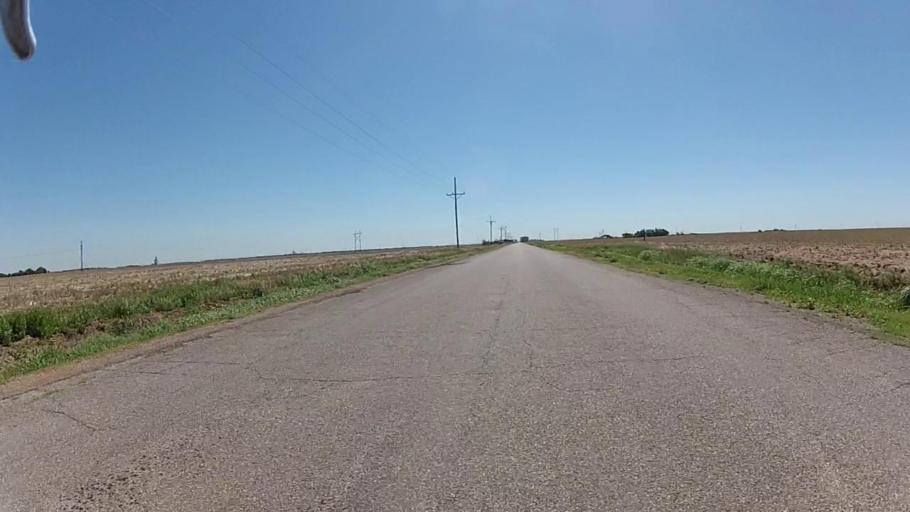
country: US
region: Kansas
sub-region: Kiowa County
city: Greensburg
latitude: 37.5866
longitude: -99.3450
